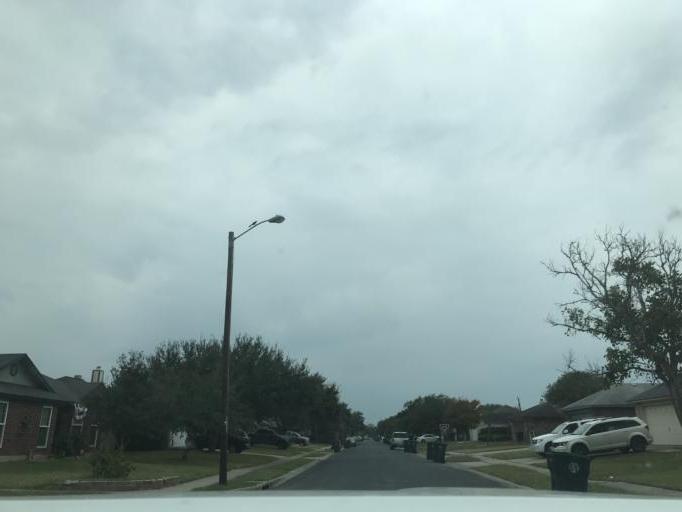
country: US
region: Texas
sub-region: Nueces County
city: Corpus Christi
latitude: 27.6700
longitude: -97.3452
